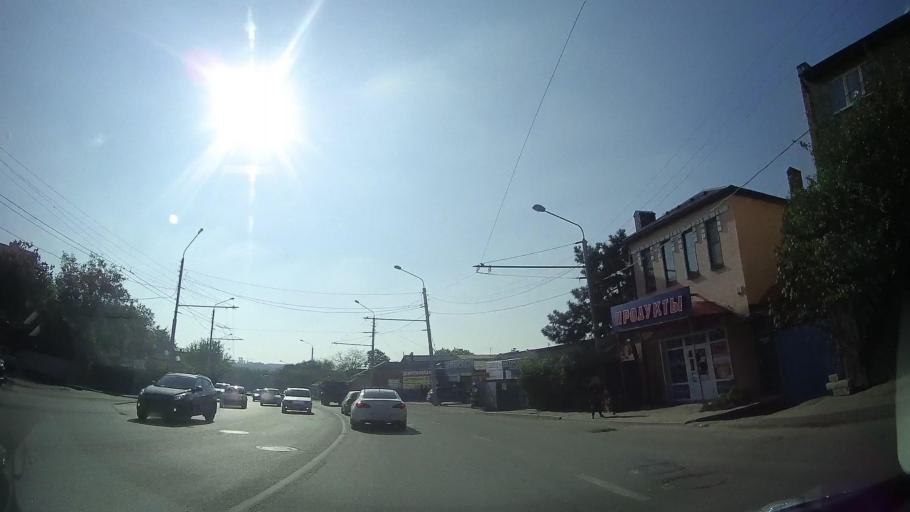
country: RU
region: Rostov
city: Severnyy
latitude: 47.2647
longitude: 39.6824
